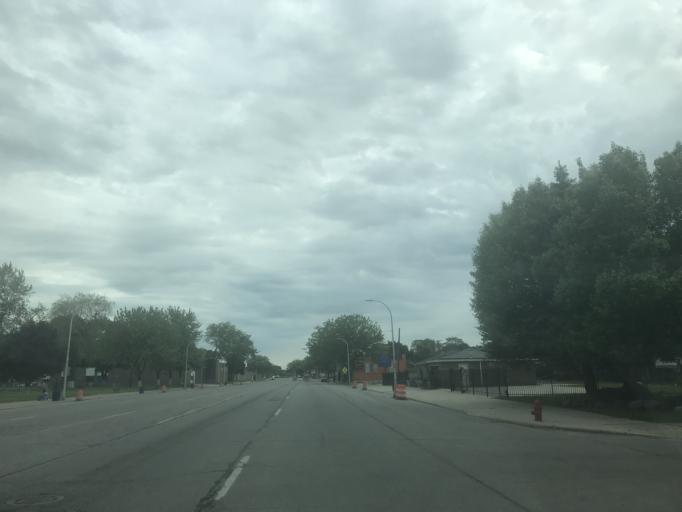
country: US
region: Michigan
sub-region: Wayne County
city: River Rouge
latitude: 42.2667
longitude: -83.1364
